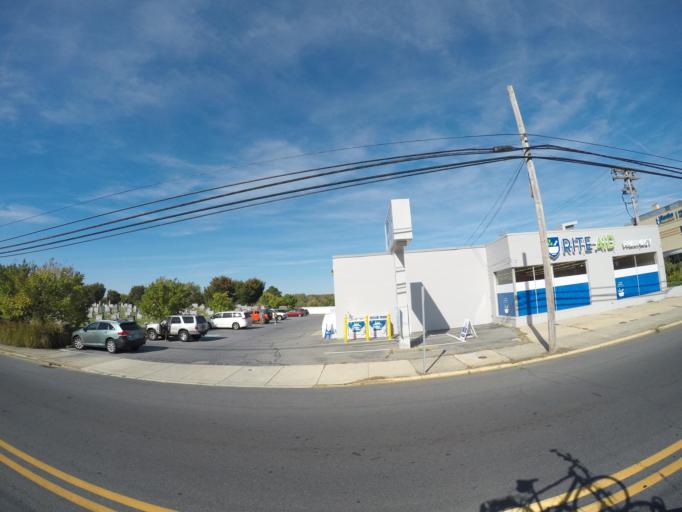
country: US
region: Delaware
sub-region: Sussex County
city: Lewes
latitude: 38.7704
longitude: -75.1434
